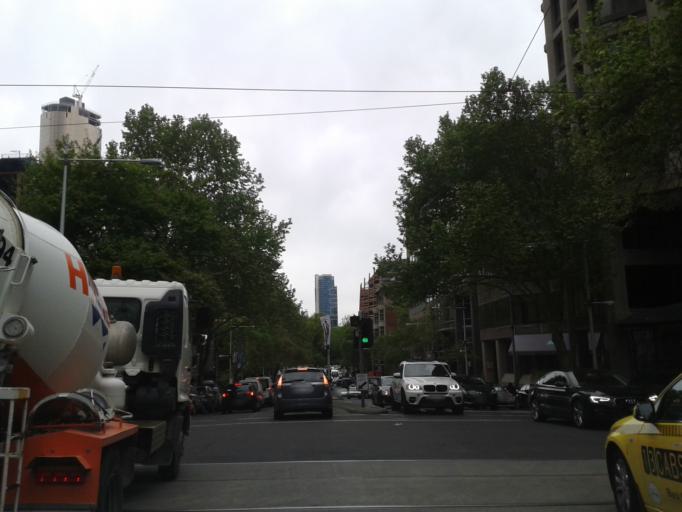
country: AU
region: Victoria
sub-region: Melbourne
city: Docklands
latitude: -37.8183
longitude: 144.9565
